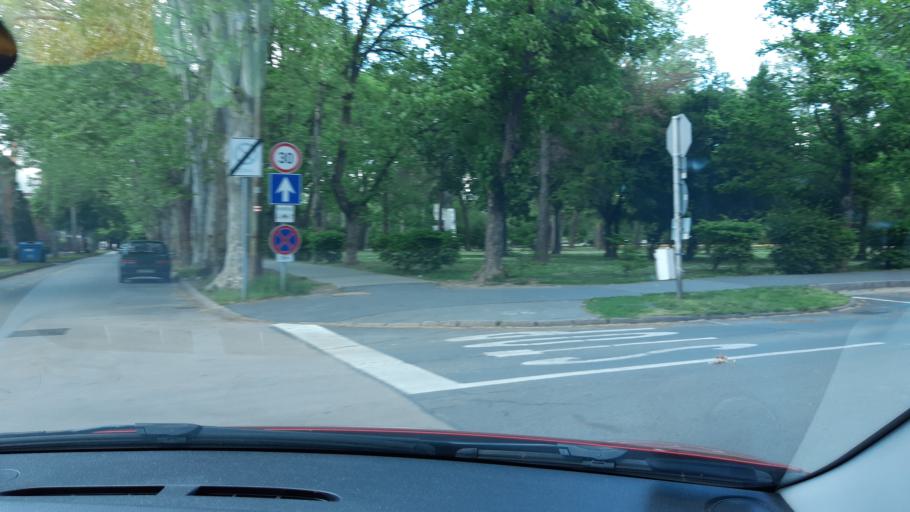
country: HU
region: Somogy
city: Kaposvar
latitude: 46.3618
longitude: 17.7908
